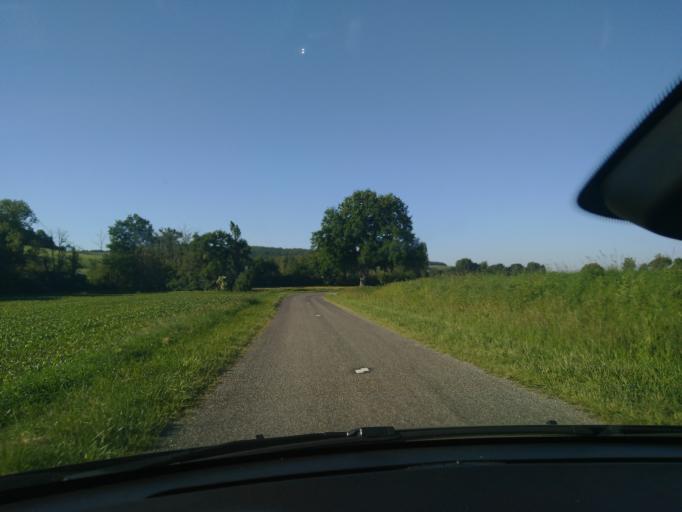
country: FR
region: Midi-Pyrenees
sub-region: Departement du Tarn-et-Garonne
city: Beaumont-de-Lomagne
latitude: 43.8358
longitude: 1.0693
